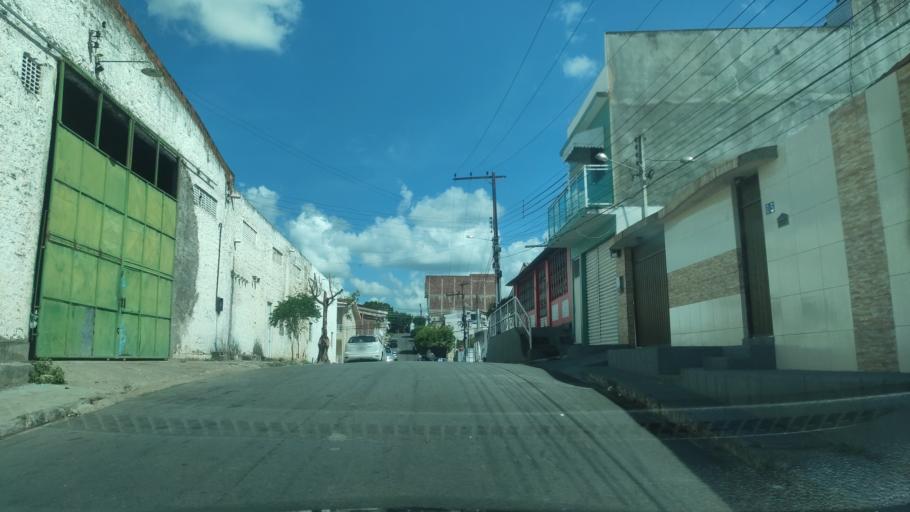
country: BR
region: Alagoas
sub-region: Uniao Dos Palmares
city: Uniao dos Palmares
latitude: -9.1602
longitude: -36.0352
